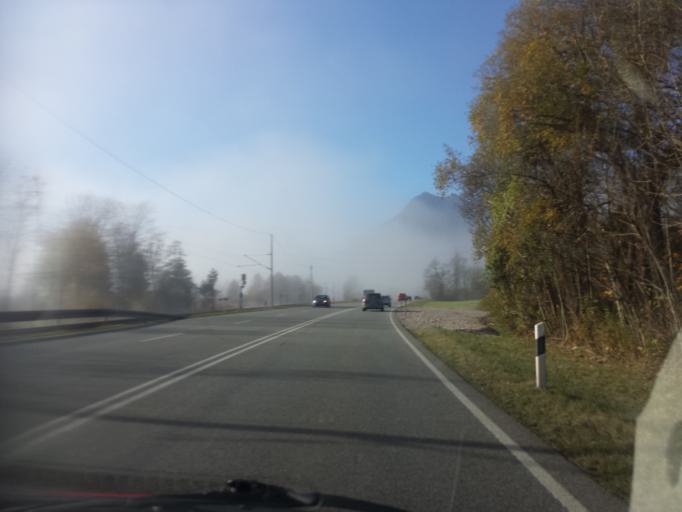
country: DE
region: Bavaria
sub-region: Upper Bavaria
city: Oberau
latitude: 47.5505
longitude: 11.1298
